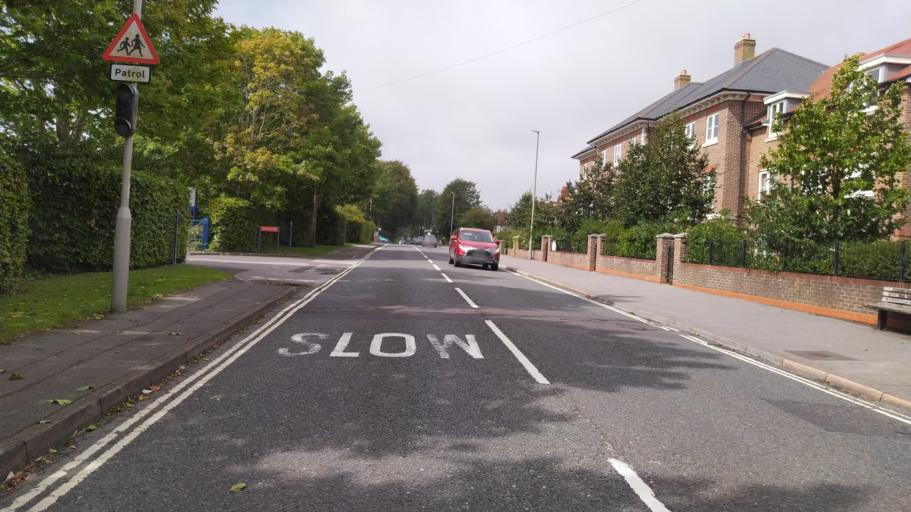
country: GB
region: England
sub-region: Dorset
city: Dorchester
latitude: 50.7136
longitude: -2.4488
